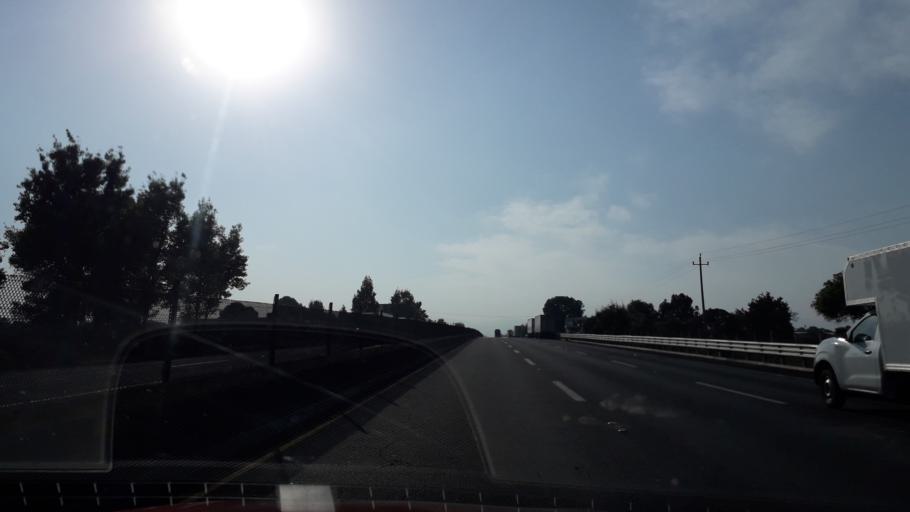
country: MX
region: Puebla
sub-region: Tlahuapan
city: Guadalupe Zaragoza
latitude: 19.3275
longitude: -98.5333
